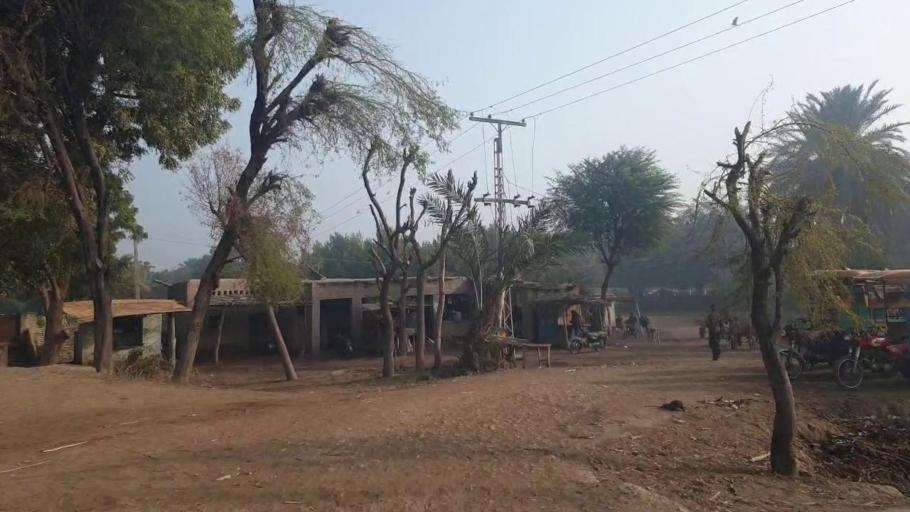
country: PK
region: Sindh
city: Tando Adam
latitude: 25.8107
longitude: 68.6315
